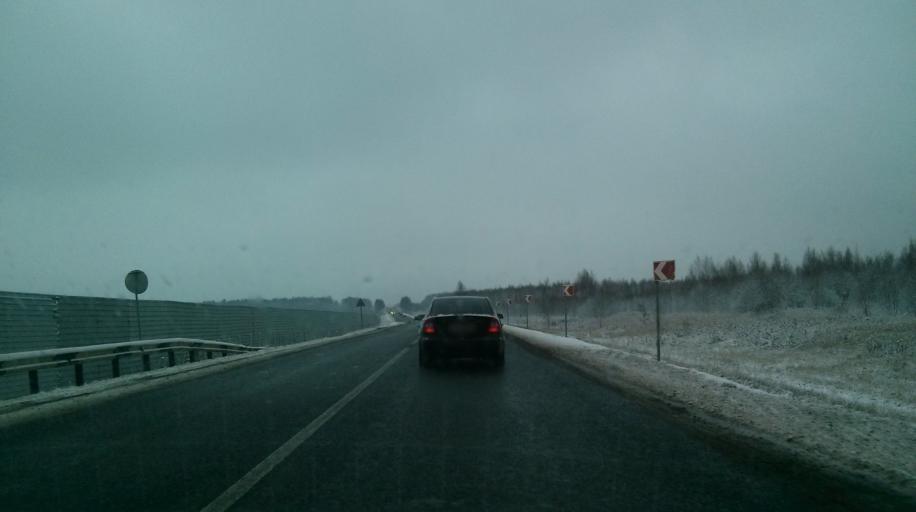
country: RU
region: Nizjnij Novgorod
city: Bogorodsk
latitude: 56.1227
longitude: 43.5967
